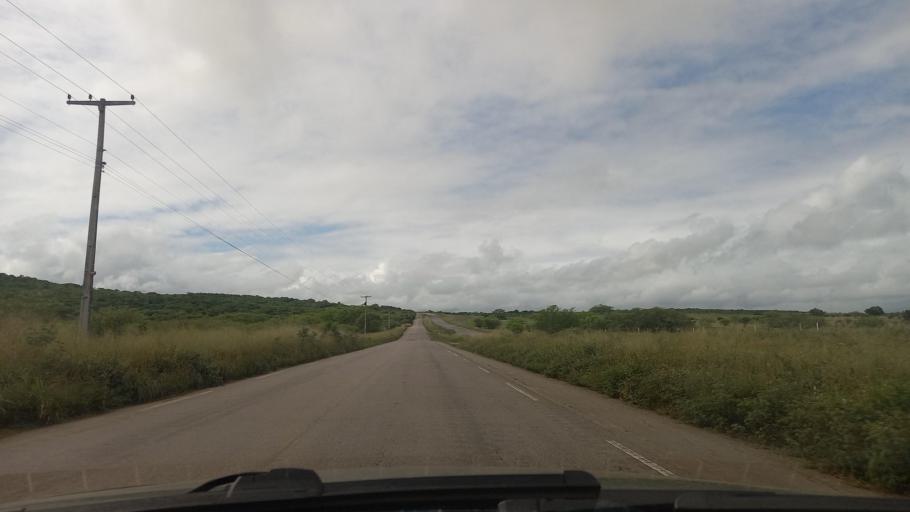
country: BR
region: Alagoas
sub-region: Batalha
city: Batalha
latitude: -9.6573
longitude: -37.1759
